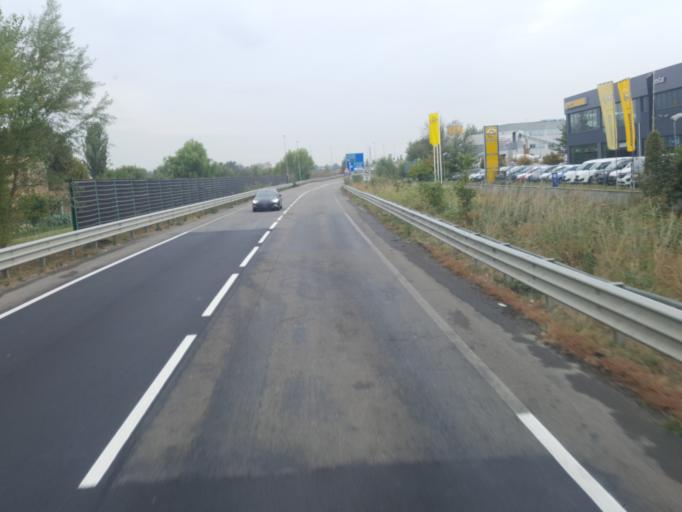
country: IT
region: Emilia-Romagna
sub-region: Provincia di Modena
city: Albareto
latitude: 44.6522
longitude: 10.9677
